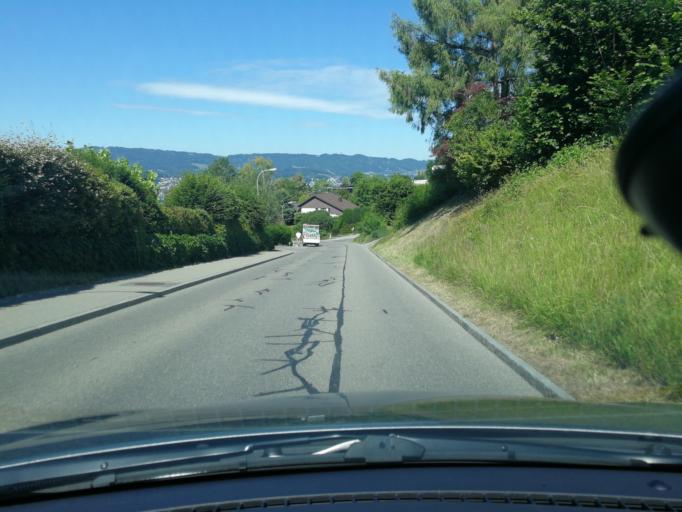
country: CH
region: Zurich
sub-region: Bezirk Meilen
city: Herrliberg
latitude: 47.2943
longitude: 8.6156
